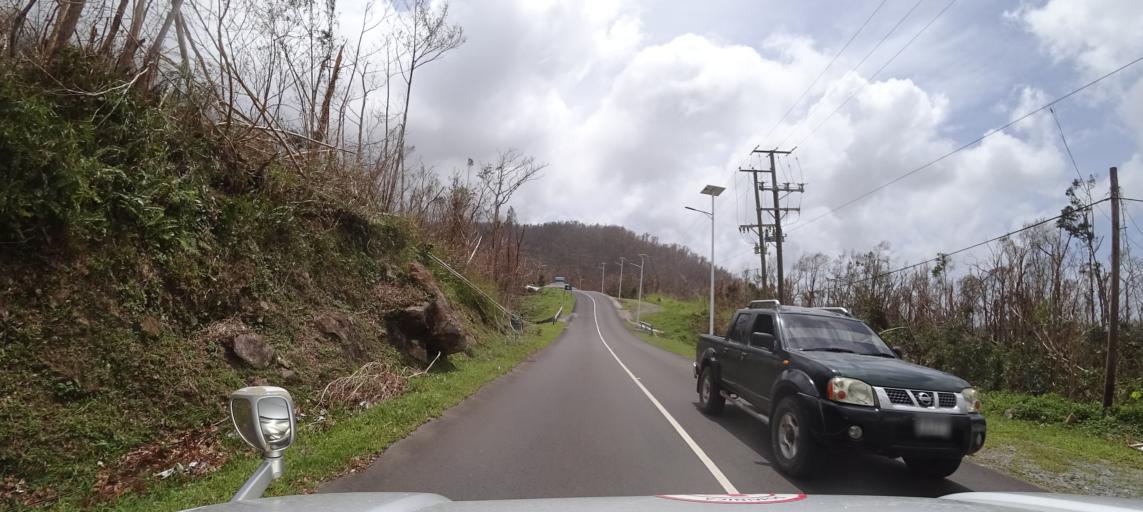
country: DM
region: Saint Paul
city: Pont Casse
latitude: 15.3791
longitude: -61.3443
